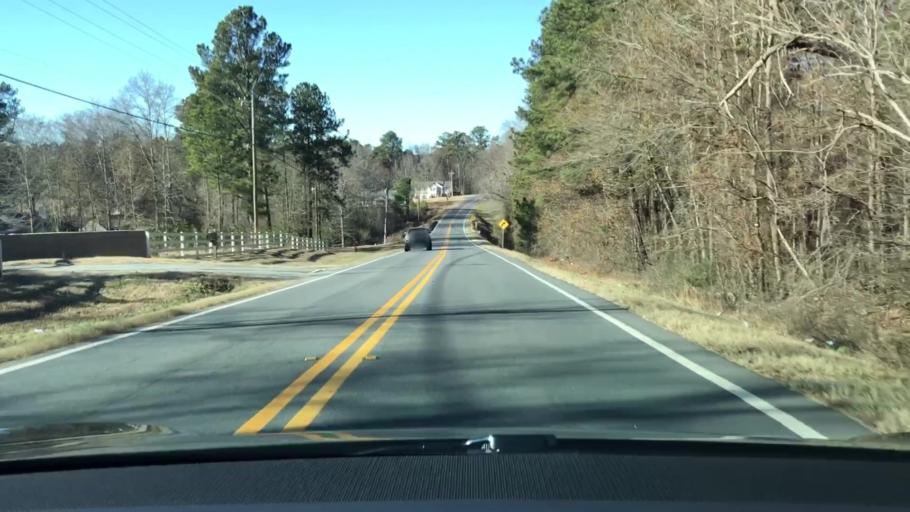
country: US
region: Georgia
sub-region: Barrow County
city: Auburn
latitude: 33.9795
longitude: -83.7926
